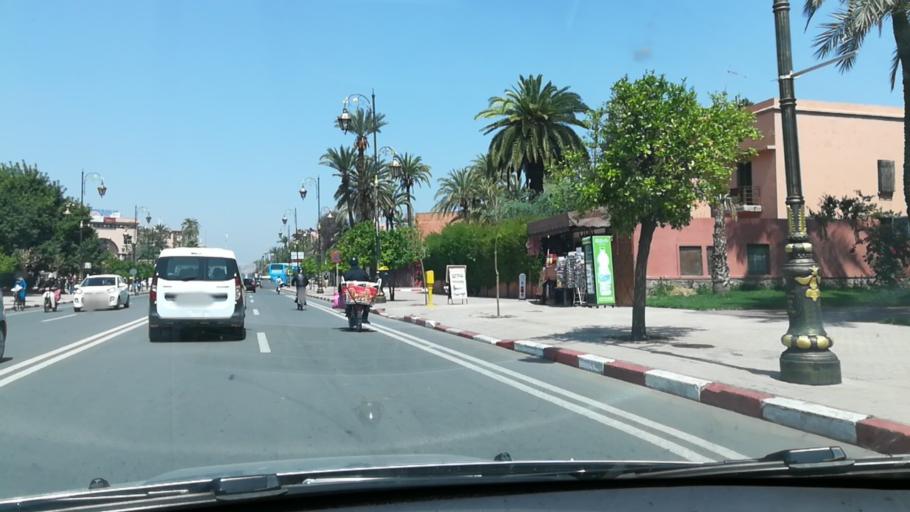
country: MA
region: Marrakech-Tensift-Al Haouz
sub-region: Marrakech
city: Marrakesh
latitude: 31.6289
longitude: -8.0017
